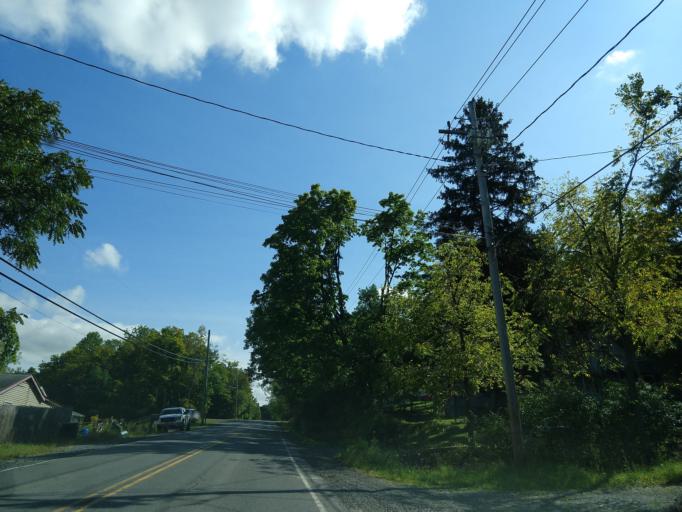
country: US
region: New York
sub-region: Tompkins County
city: South Hill
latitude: 42.4247
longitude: -76.4869
